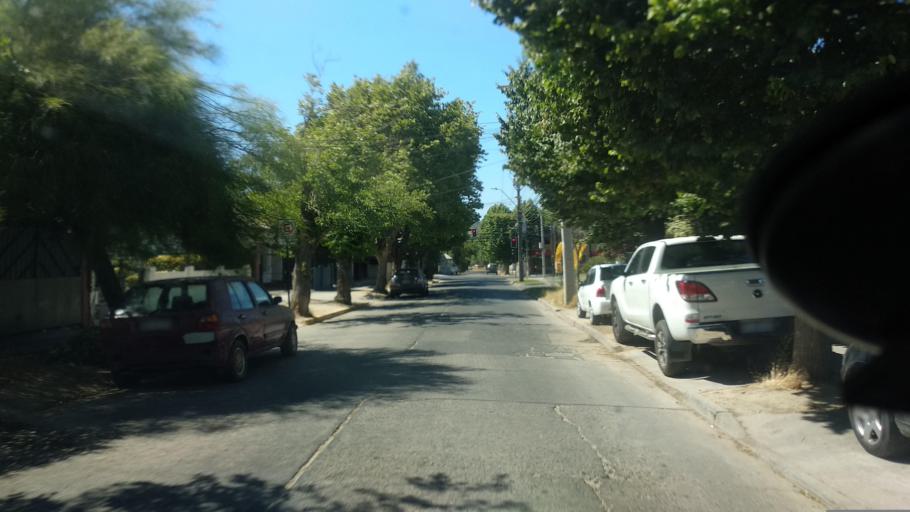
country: CL
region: Valparaiso
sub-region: Provincia de Marga Marga
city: Villa Alemana
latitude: -33.0450
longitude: -71.3687
